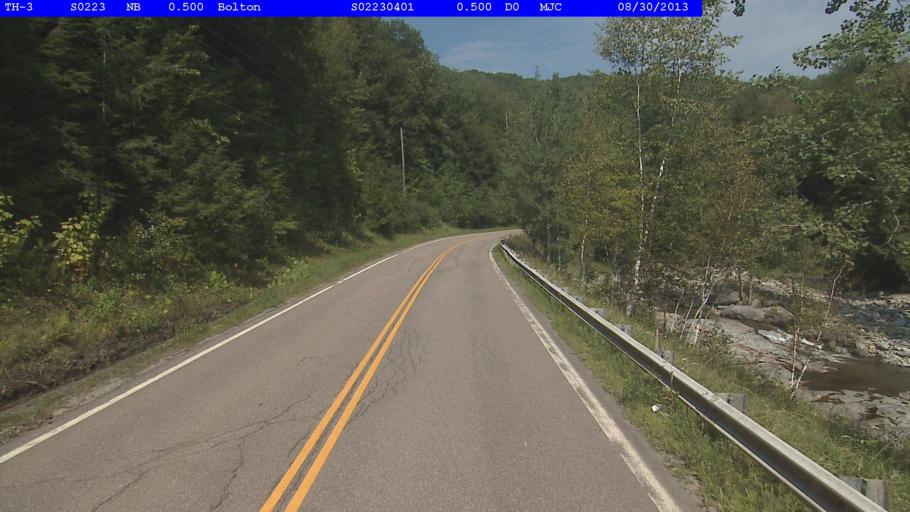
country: US
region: Vermont
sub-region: Washington County
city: Waterbury
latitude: 44.3785
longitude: -72.8756
